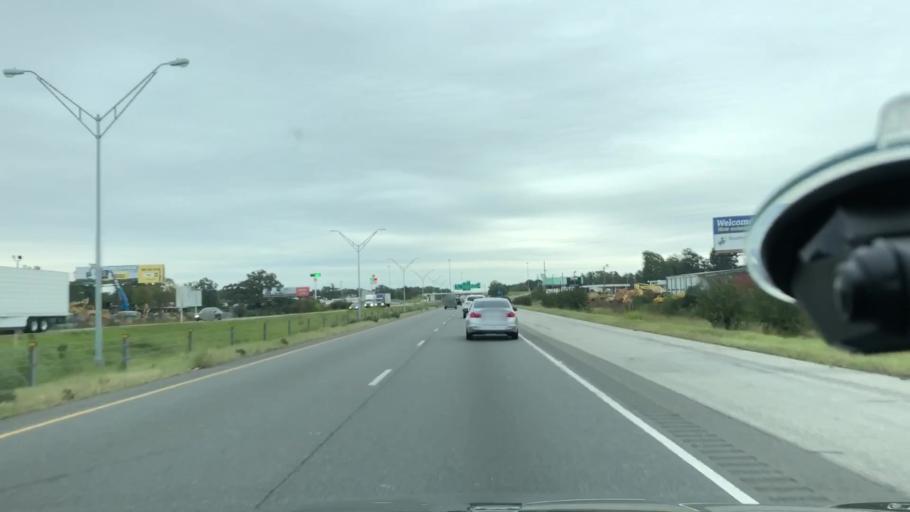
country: US
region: Arkansas
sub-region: Miller County
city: Texarkana
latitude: 33.4740
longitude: -94.0156
